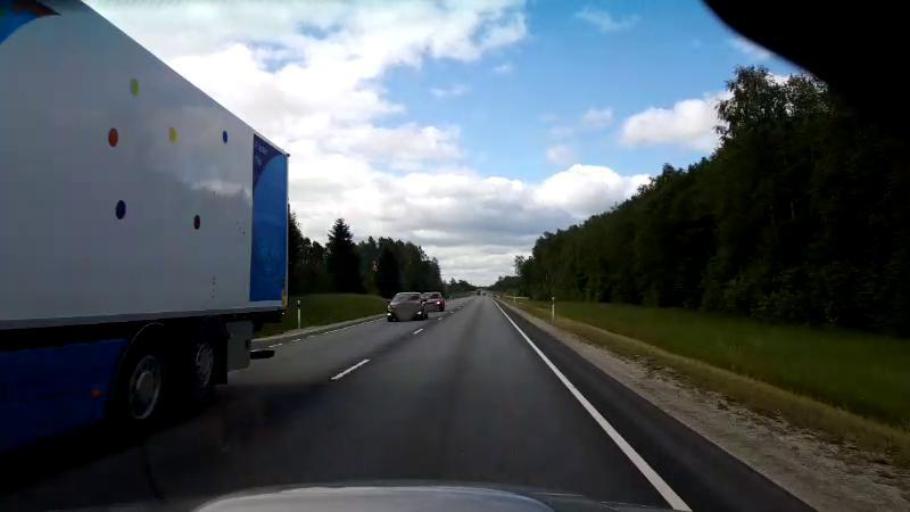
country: EE
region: Harju
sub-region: Nissi vald
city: Riisipere
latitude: 59.0694
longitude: 24.4515
